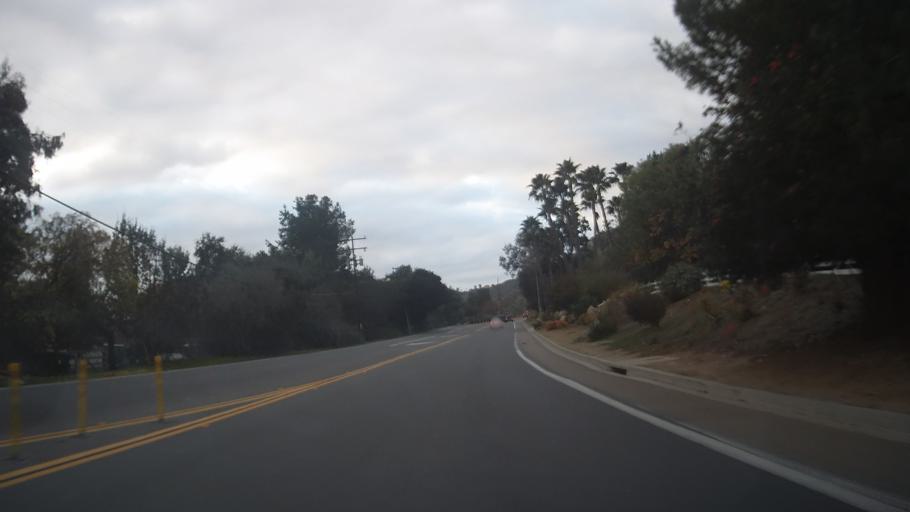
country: US
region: California
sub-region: San Diego County
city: Crest
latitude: 32.7807
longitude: -116.8731
